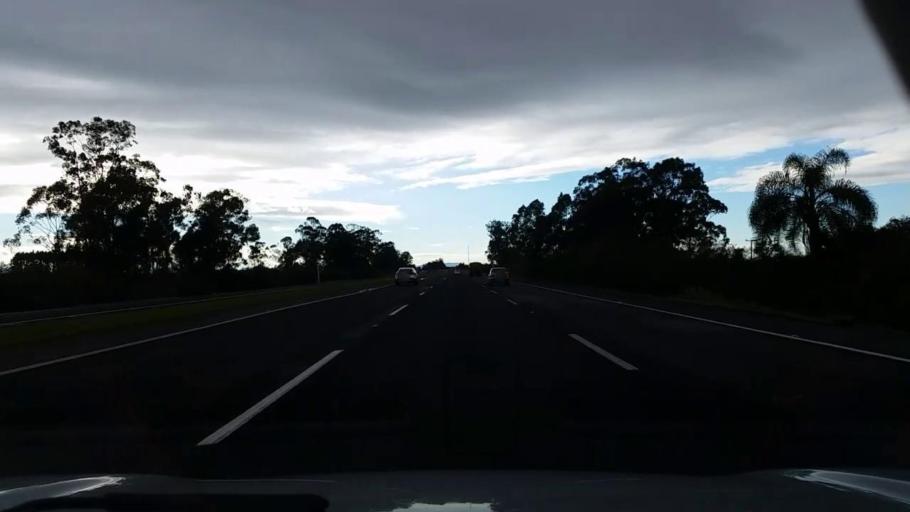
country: BR
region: Rio Grande do Sul
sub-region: Taquara
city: Taquara
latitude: -29.8899
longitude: -50.6914
